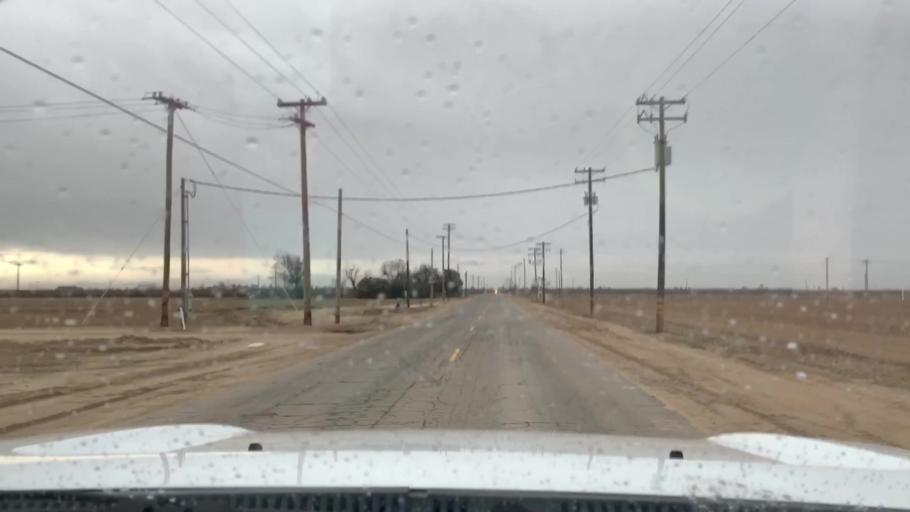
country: US
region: California
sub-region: Kern County
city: Shafter
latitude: 35.5311
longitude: -119.2779
